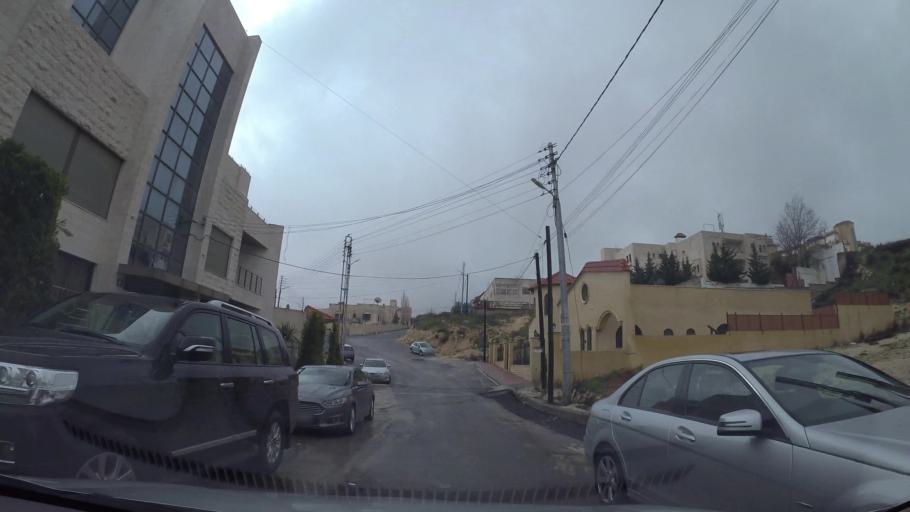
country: JO
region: Amman
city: Al Jubayhah
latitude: 32.0157
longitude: 35.8306
